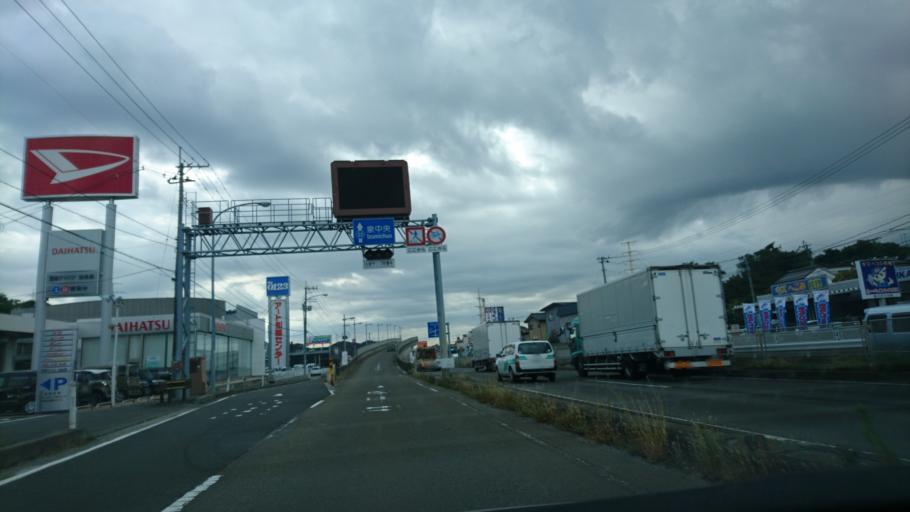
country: JP
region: Miyagi
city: Tomiya
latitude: 38.3395
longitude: 140.8846
